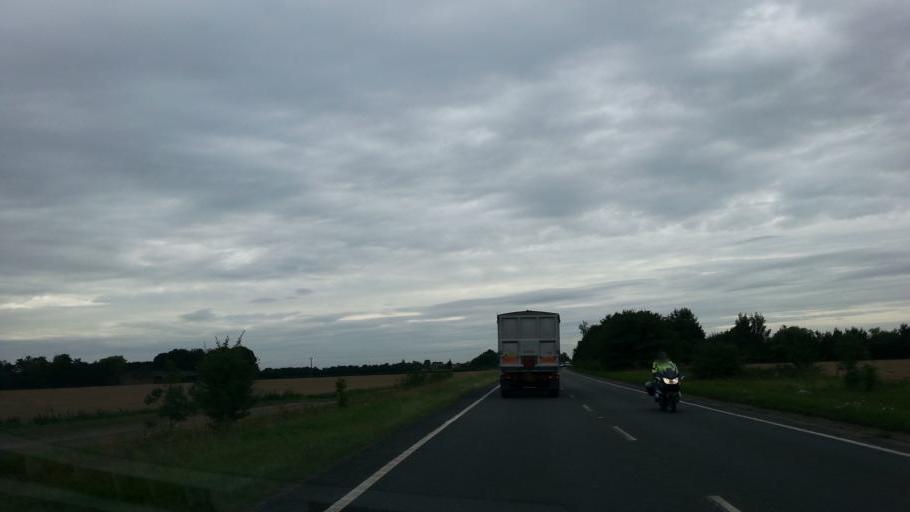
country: GB
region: England
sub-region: Peterborough
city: Eye
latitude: 52.6140
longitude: -0.1647
